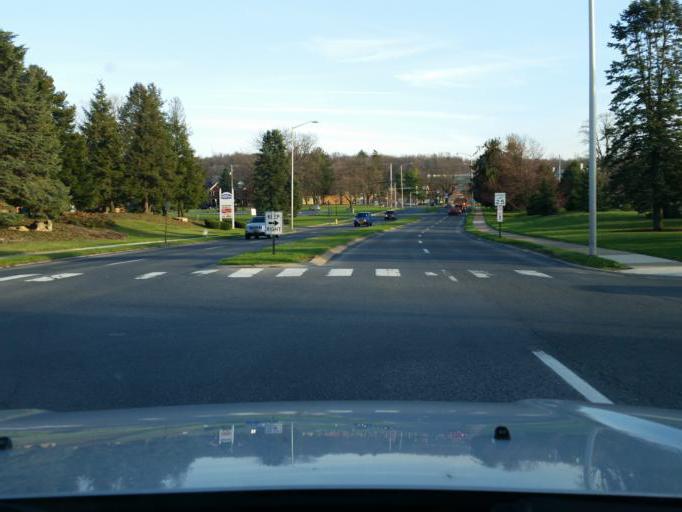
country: US
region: Pennsylvania
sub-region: Dauphin County
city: Hershey
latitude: 40.2703
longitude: -76.6744
